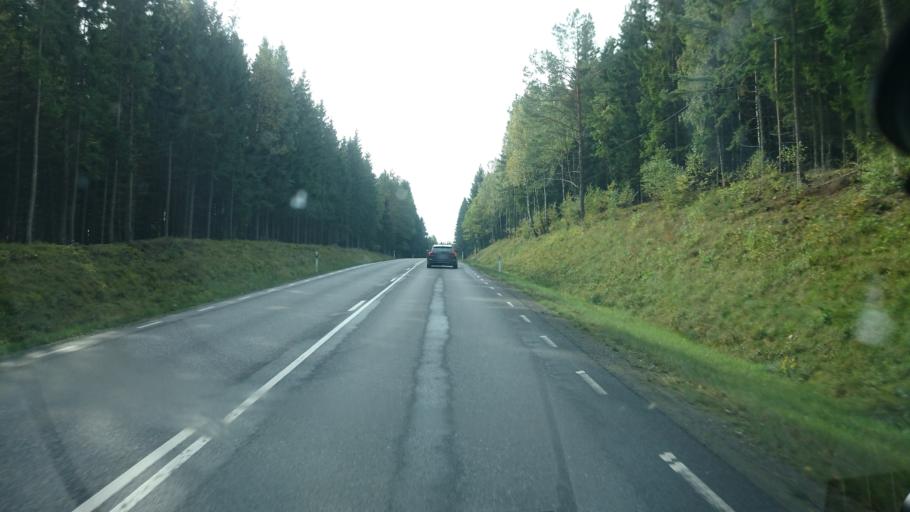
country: SE
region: Vaestra Goetaland
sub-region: Alingsas Kommun
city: Sollebrunn
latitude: 58.0289
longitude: 12.4622
